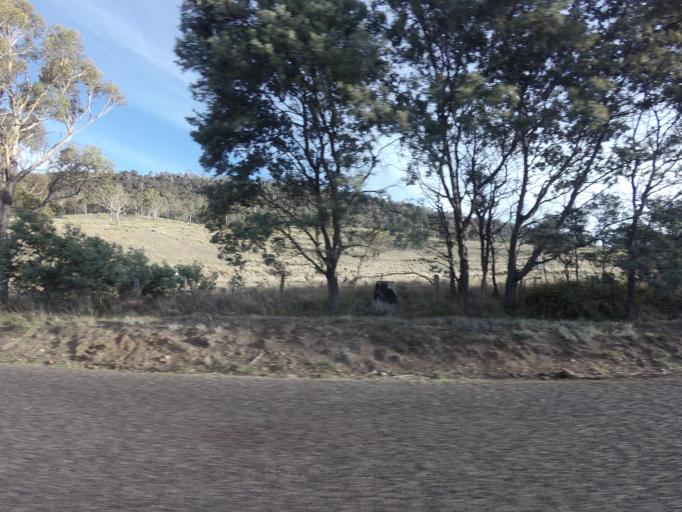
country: AU
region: Tasmania
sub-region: Brighton
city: Bridgewater
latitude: -42.4061
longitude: 147.1120
